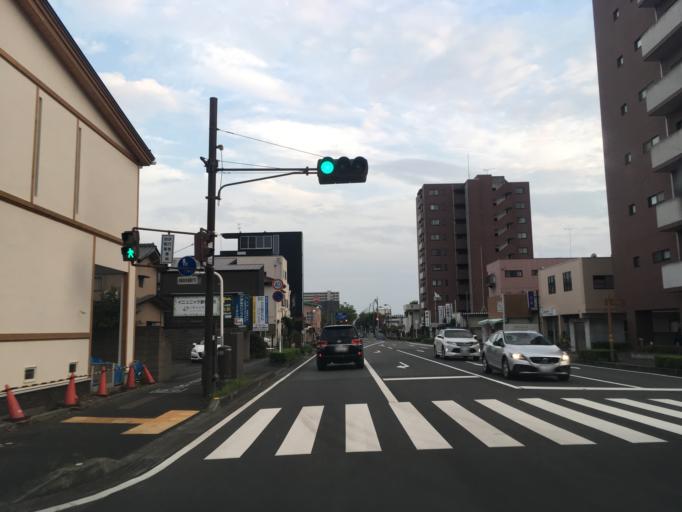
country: JP
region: Gunma
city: Maebashi-shi
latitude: 36.3824
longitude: 139.0765
